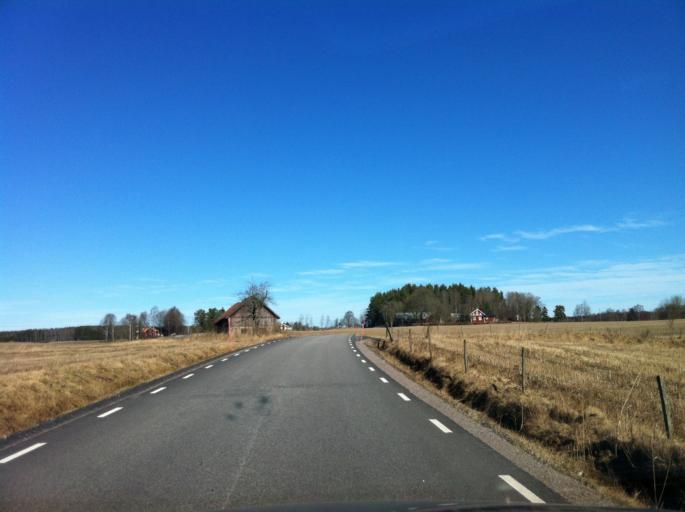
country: SE
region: Vaestra Goetaland
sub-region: Toreboda Kommun
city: Toereboda
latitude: 58.7384
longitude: 14.1290
